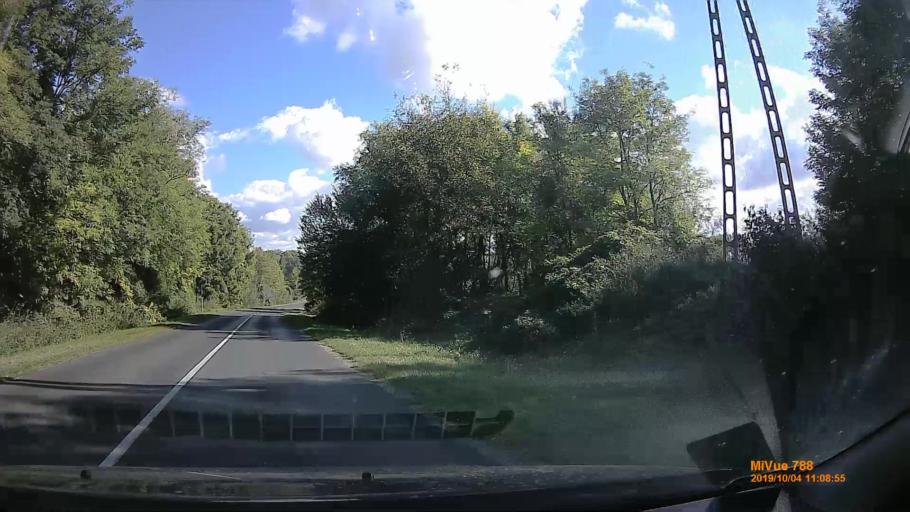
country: HU
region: Somogy
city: Kaposmero
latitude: 46.4114
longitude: 17.7419
